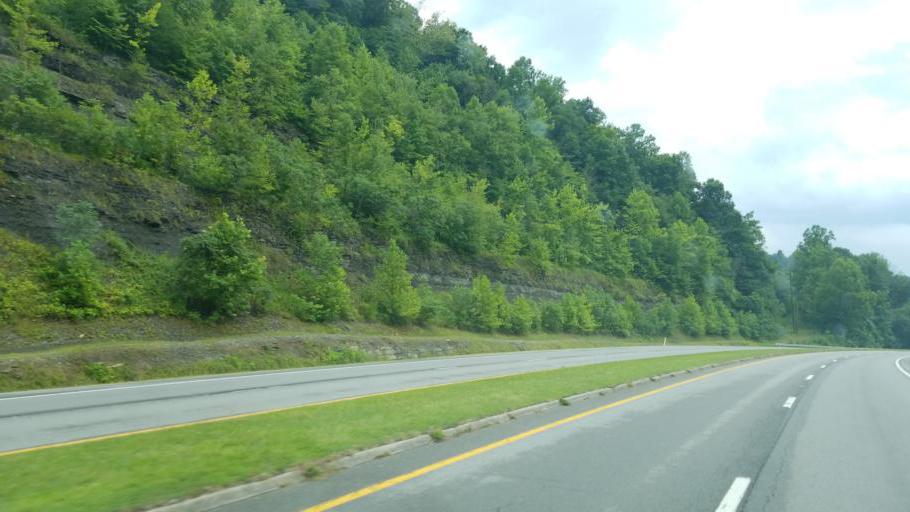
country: US
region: West Virginia
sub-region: Mingo County
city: Williamson
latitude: 37.7614
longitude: -82.3091
